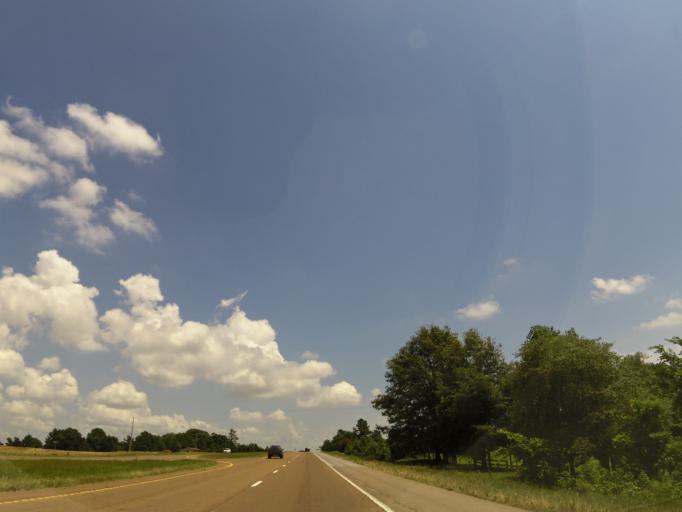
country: US
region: Tennessee
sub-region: Lauderdale County
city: Halls
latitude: 35.9409
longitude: -89.2988
